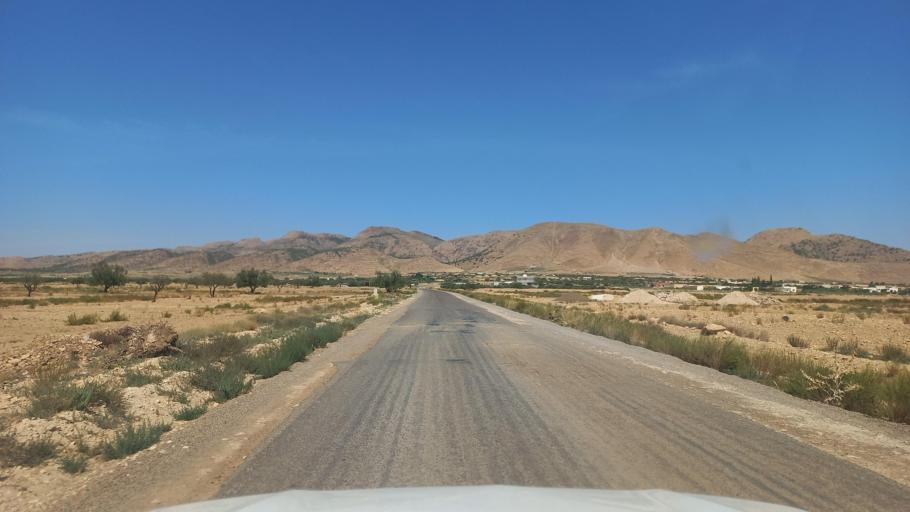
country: TN
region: Al Qasrayn
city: Sbiba
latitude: 35.4392
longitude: 9.0771
